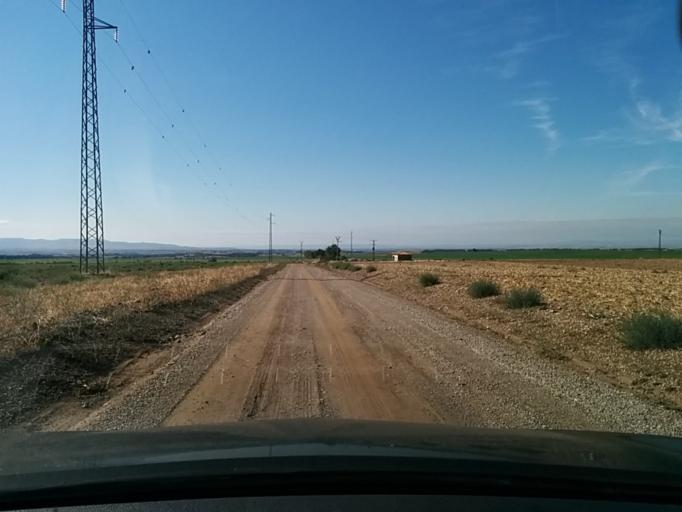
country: ES
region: Aragon
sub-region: Provincia de Zaragoza
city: Tauste
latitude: 42.0060
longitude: -1.2990
